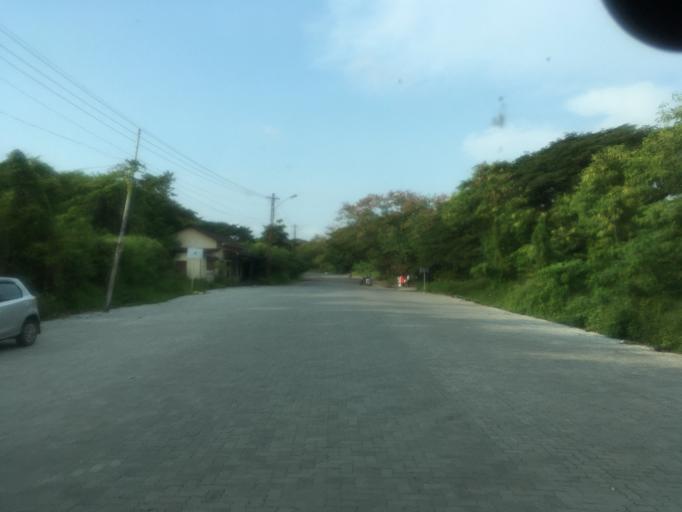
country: IN
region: Kerala
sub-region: Ernakulam
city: Cochin
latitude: 9.9549
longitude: 76.2684
